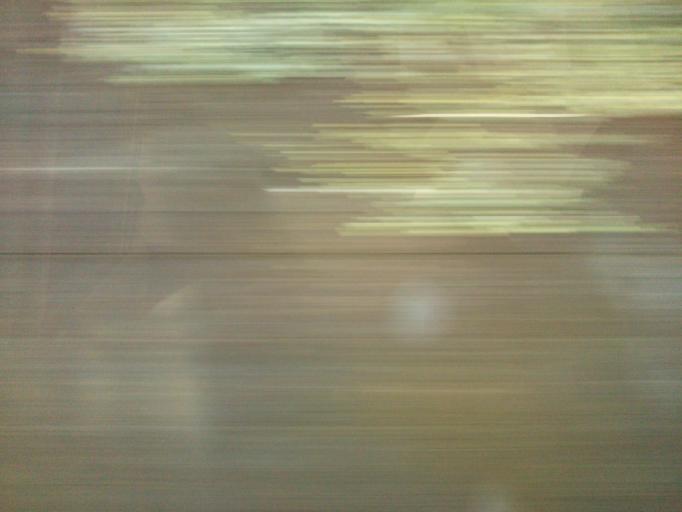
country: JP
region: Kochi
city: Nakamura
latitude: 33.0571
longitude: 133.0975
